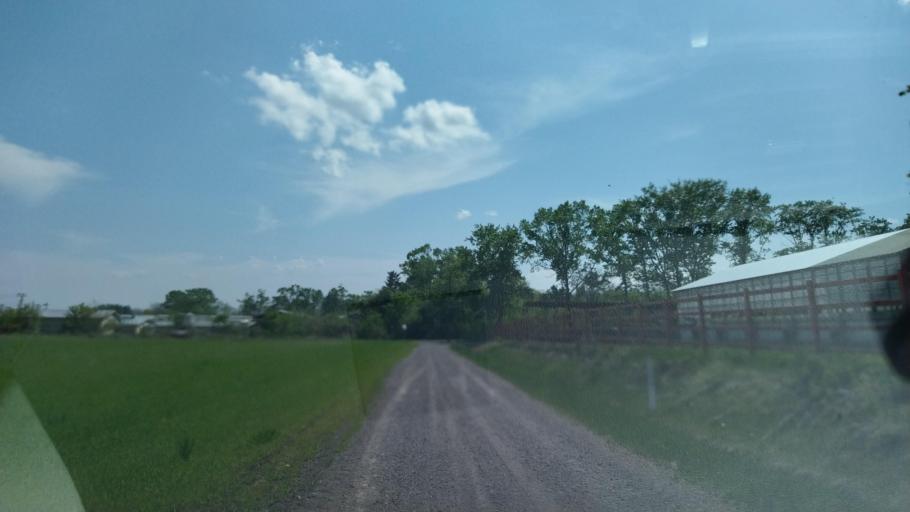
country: JP
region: Hokkaido
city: Otofuke
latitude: 43.1333
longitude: 143.2181
